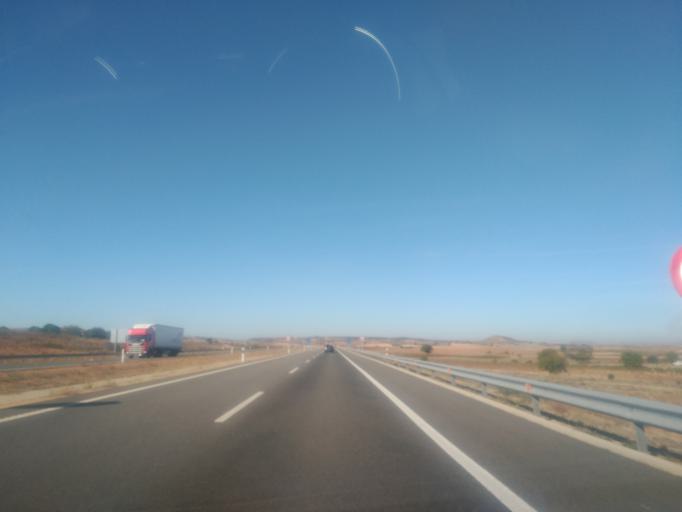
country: ES
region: Castille and Leon
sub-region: Provincia de Burgos
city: Castrillo de la Vega
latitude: 41.6346
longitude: -3.7690
